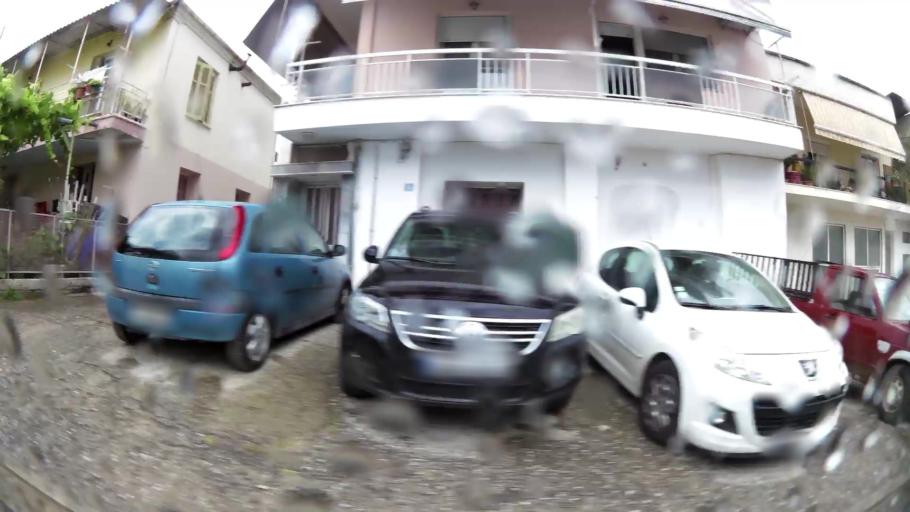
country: GR
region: Central Macedonia
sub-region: Nomos Imathias
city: Veroia
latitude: 40.5329
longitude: 22.2048
